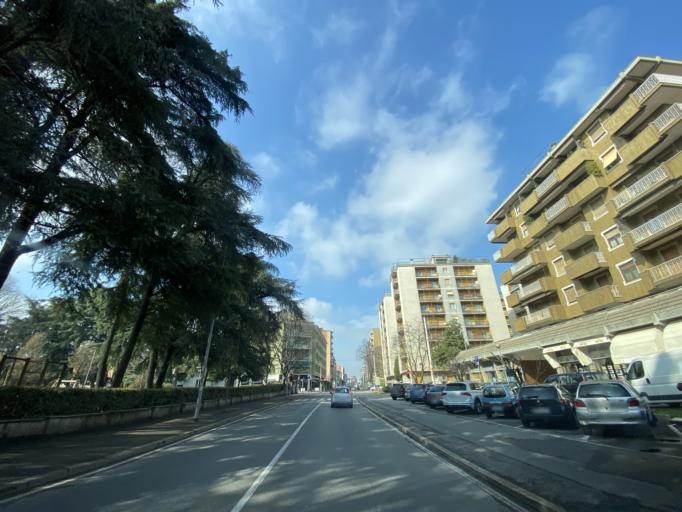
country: IT
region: Lombardy
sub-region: Citta metropolitana di Milano
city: Bresso
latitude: 45.5366
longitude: 9.1921
